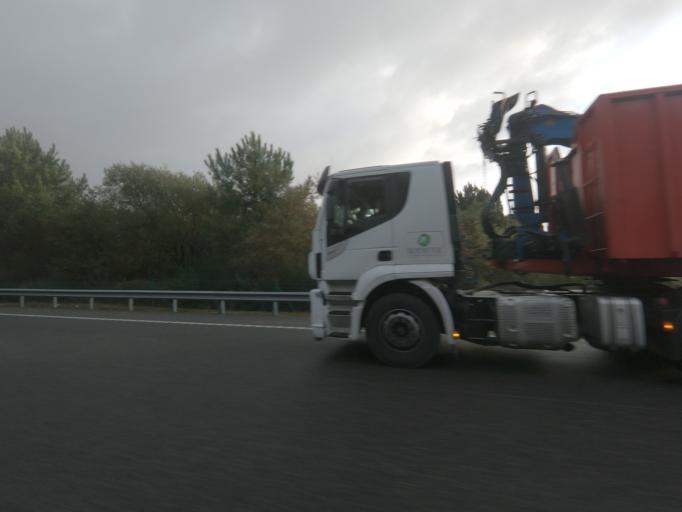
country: ES
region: Galicia
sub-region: Provincia de Pontevedra
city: Porrino
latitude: 42.1793
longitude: -8.6504
